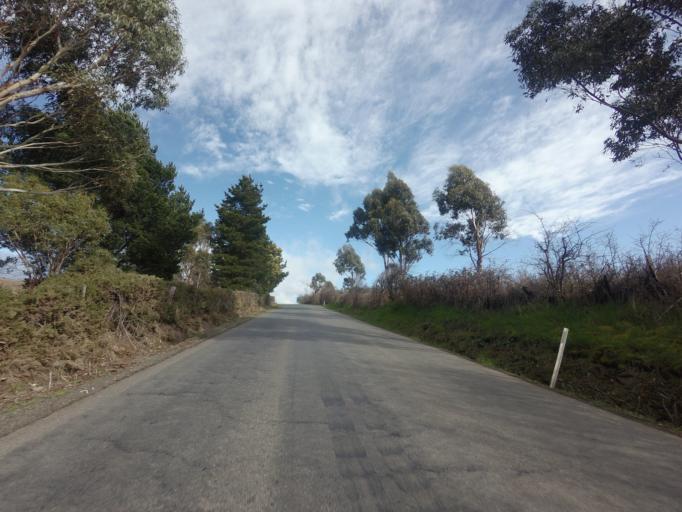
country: AU
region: Tasmania
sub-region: Derwent Valley
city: New Norfolk
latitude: -42.7750
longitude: 147.0211
